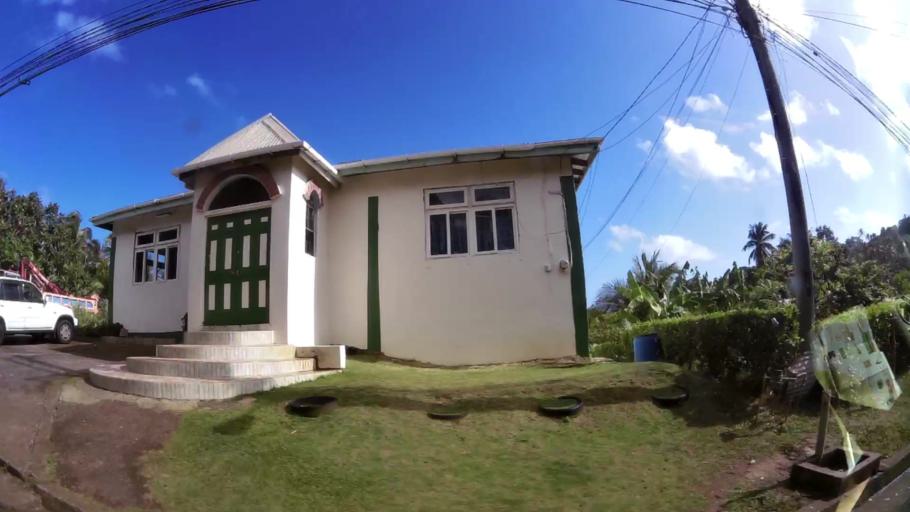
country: DM
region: Saint Andrew
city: Marigot
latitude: 15.5358
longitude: -61.2777
